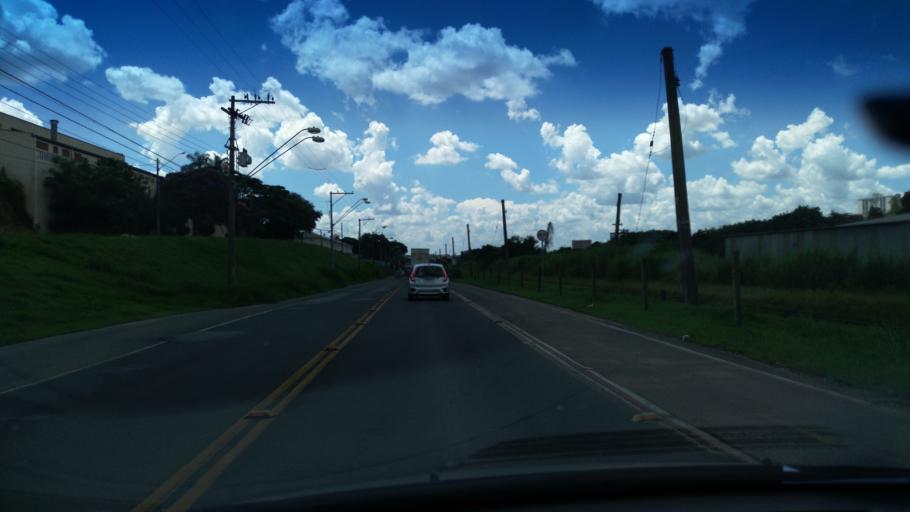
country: BR
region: Sao Paulo
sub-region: Valinhos
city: Valinhos
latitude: -22.9960
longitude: -46.9897
